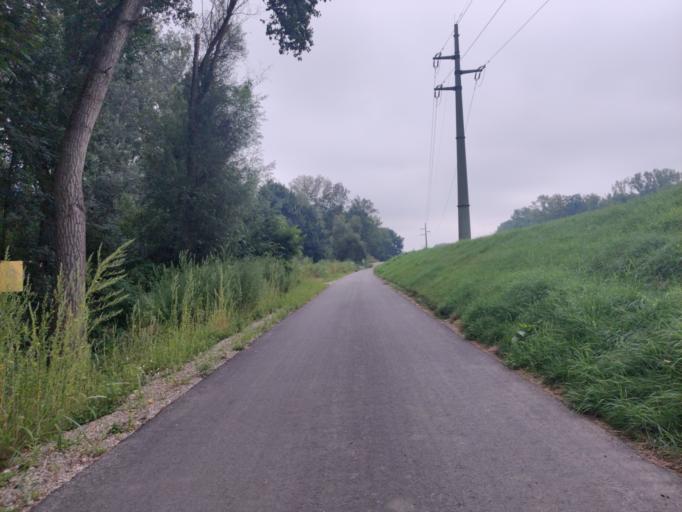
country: AT
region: Lower Austria
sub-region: Politischer Bezirk Krems
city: Gedersdorf
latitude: 48.3978
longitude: 15.6686
